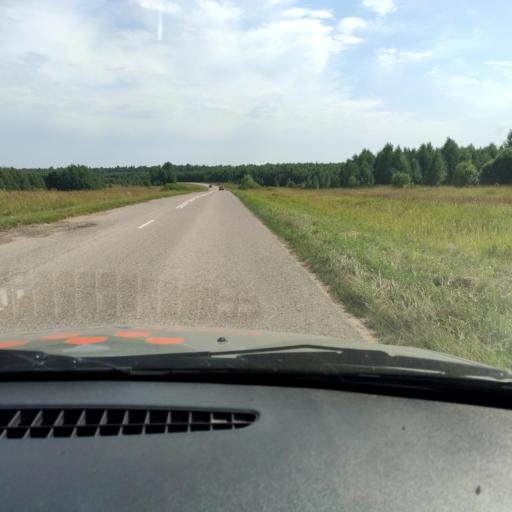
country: RU
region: Bashkortostan
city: Pavlovka
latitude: 55.3877
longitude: 56.4684
